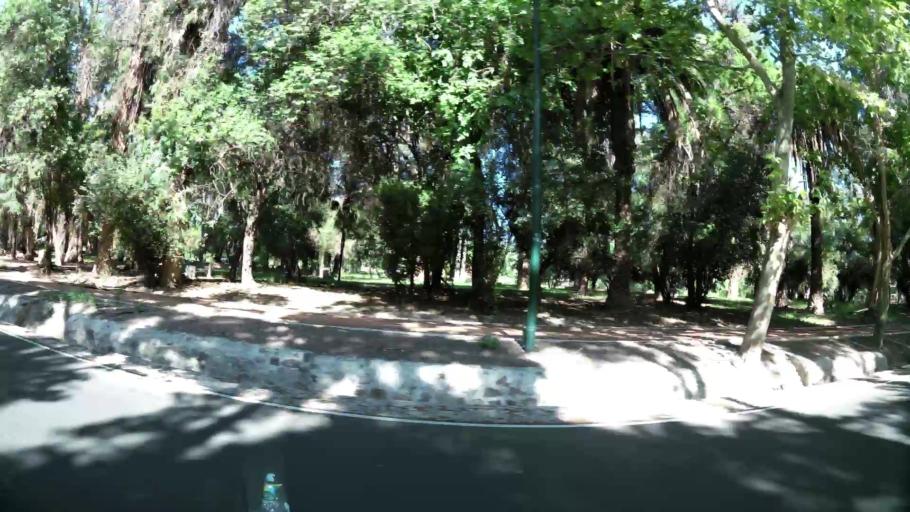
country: AR
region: Mendoza
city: Mendoza
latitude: -32.8869
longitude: -68.8731
